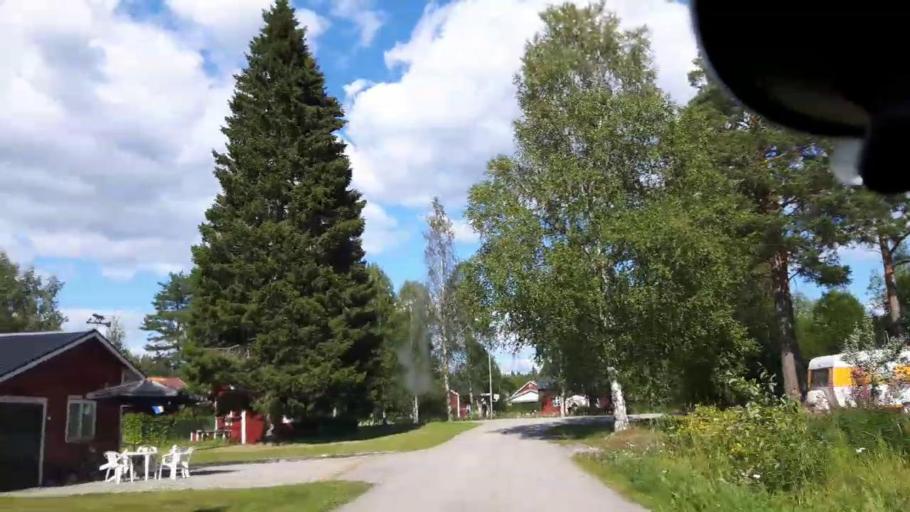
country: SE
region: Jaemtland
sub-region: Braecke Kommun
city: Braecke
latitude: 62.8317
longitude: 15.3093
